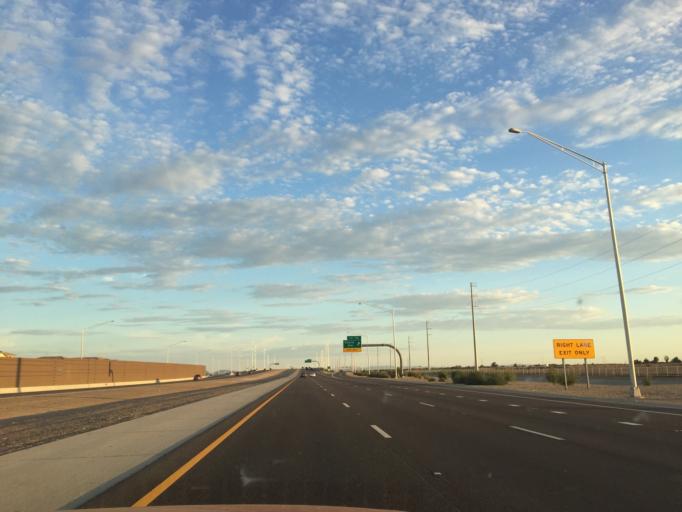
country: US
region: Arizona
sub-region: Maricopa County
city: Citrus Park
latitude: 33.5878
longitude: -112.4183
